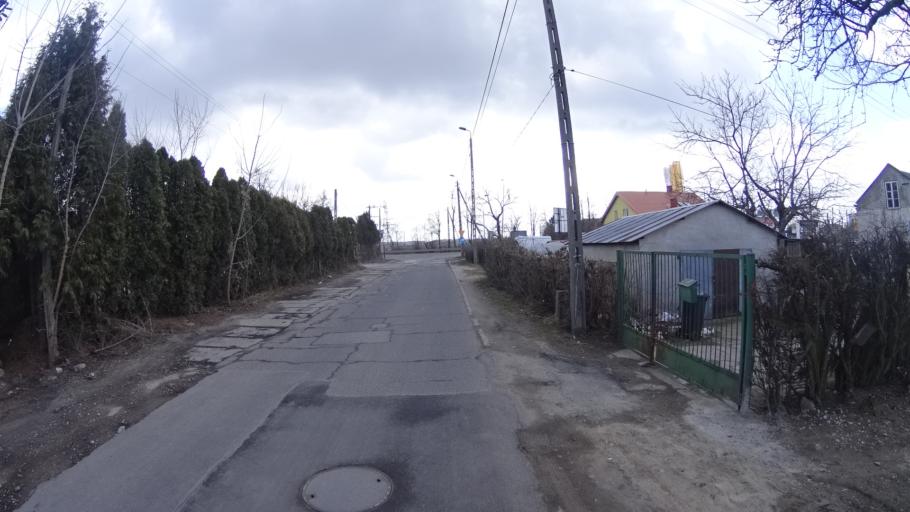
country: PL
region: Masovian Voivodeship
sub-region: Warszawa
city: Ursus
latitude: 52.2172
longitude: 20.8684
